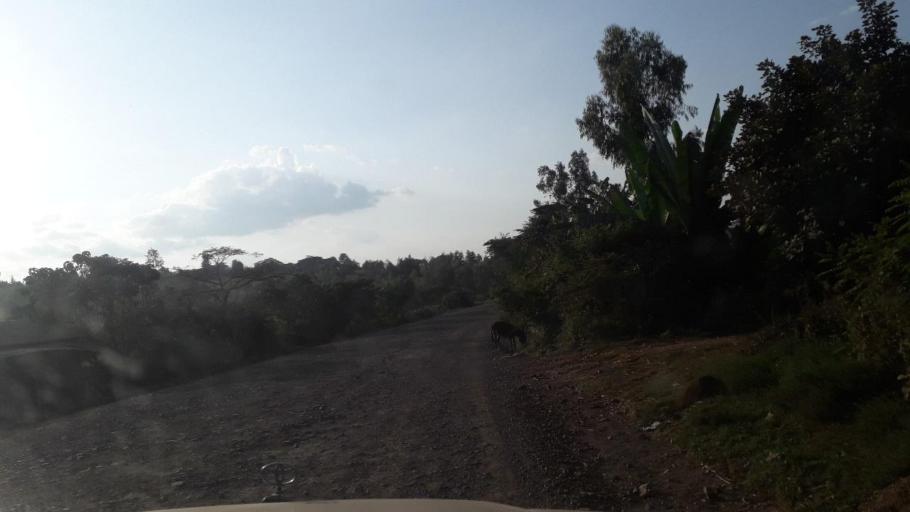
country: ET
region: Oromiya
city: Jima
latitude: 7.5931
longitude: 36.8526
